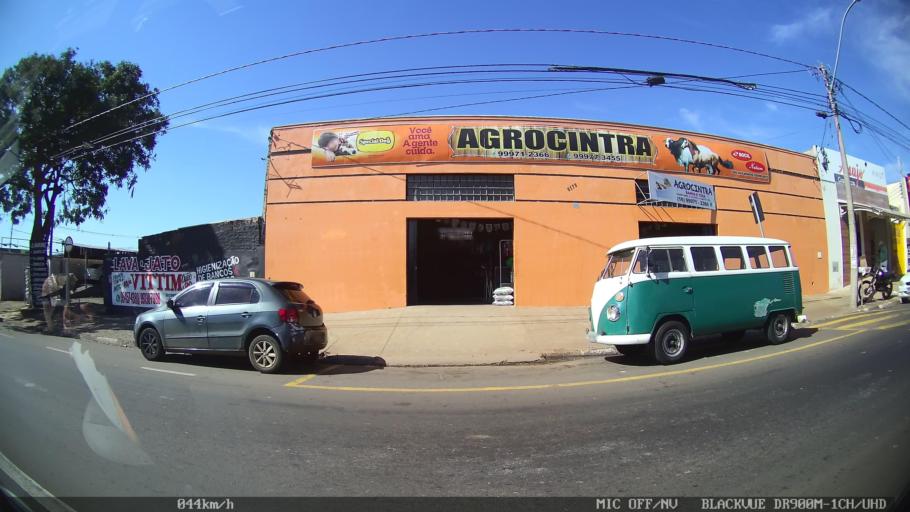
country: BR
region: Sao Paulo
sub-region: Franca
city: Franca
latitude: -20.4968
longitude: -47.3980
